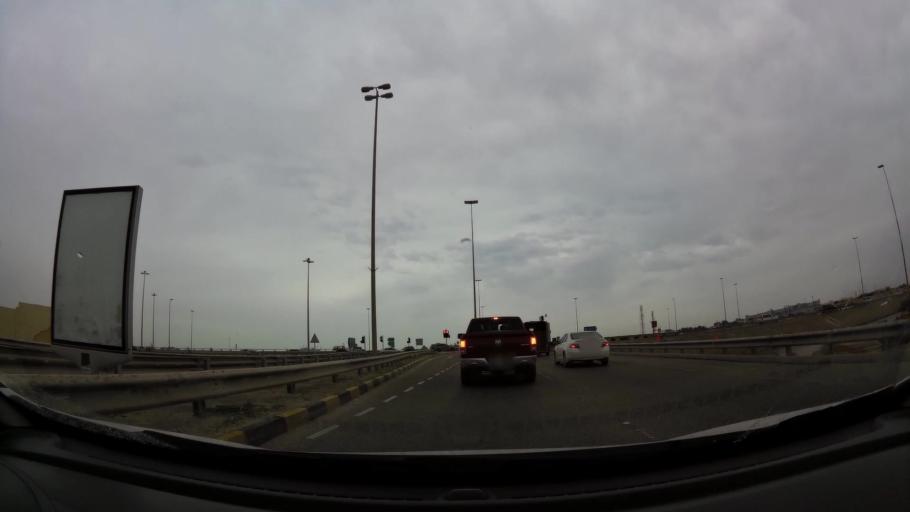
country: BH
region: Central Governorate
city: Madinat Hamad
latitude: 26.1703
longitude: 50.4654
